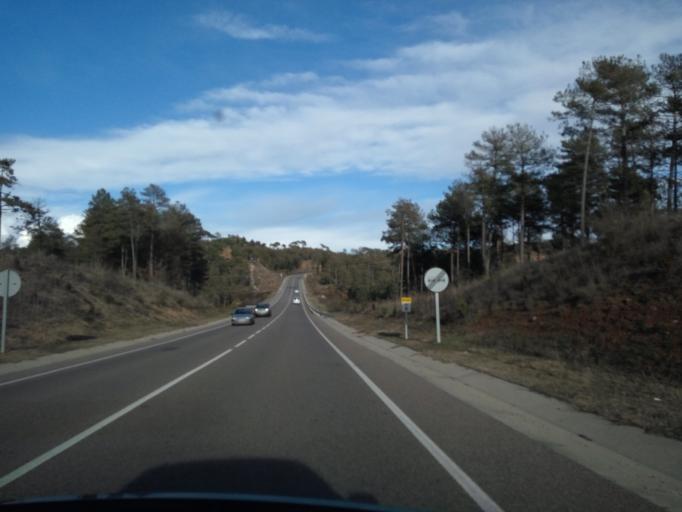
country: ES
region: Catalonia
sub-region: Provincia de Barcelona
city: Gironella
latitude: 42.0250
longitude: 1.8572
